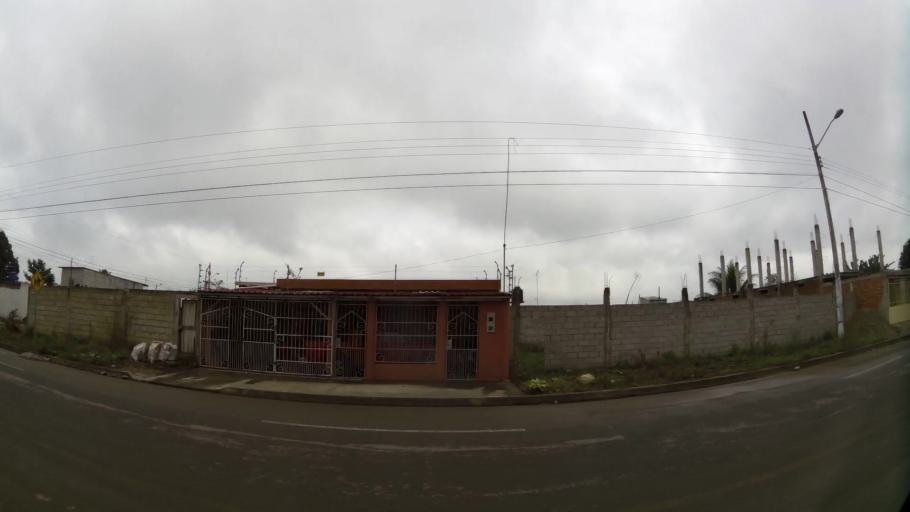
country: EC
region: El Oro
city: Pasaje
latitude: -3.3258
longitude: -79.8209
